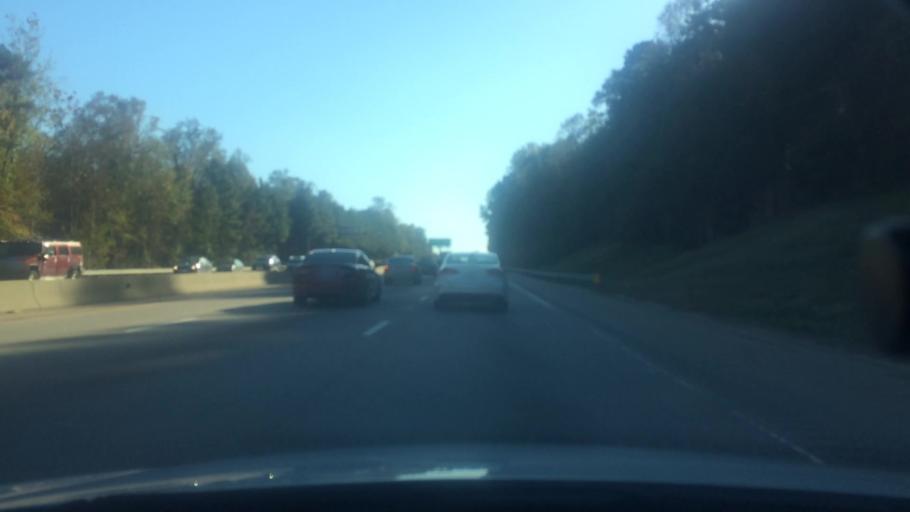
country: US
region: North Carolina
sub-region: Wake County
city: West Raleigh
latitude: 35.8239
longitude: -78.6856
